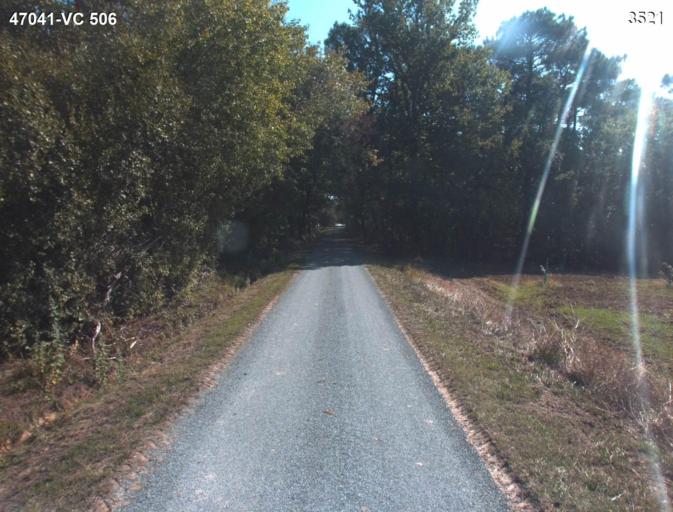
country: FR
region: Aquitaine
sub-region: Departement du Lot-et-Garonne
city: Port-Sainte-Marie
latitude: 44.1882
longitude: 0.3851
